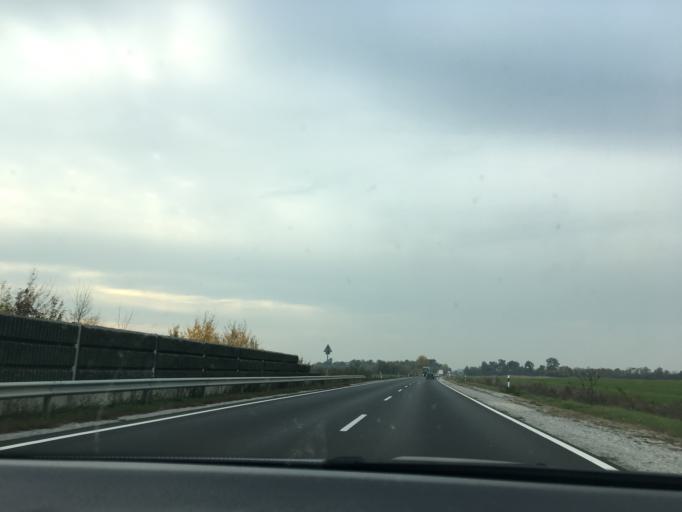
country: HU
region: Pest
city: Abony
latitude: 47.1944
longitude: 19.9325
